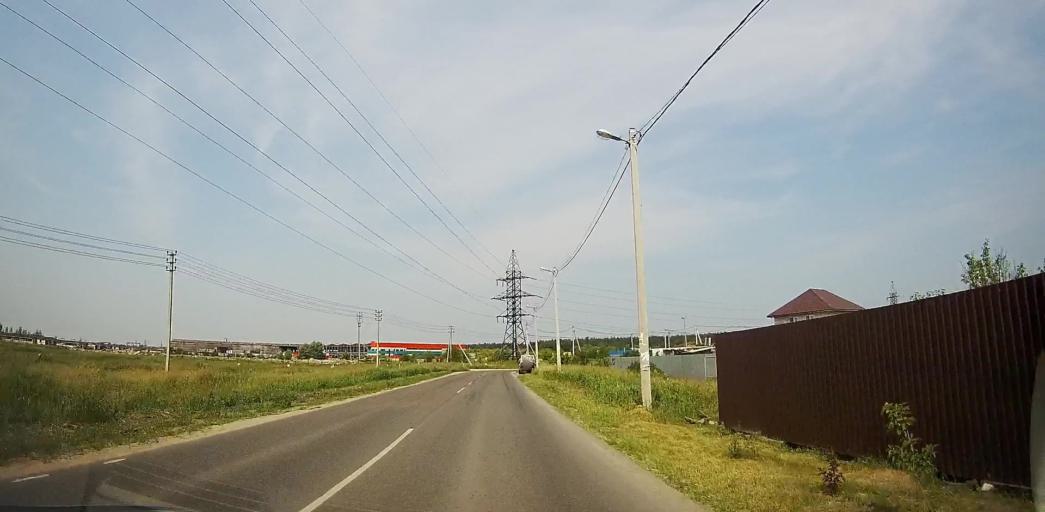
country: RU
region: Moskovskaya
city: Malyshevo
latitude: 55.5029
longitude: 38.3237
